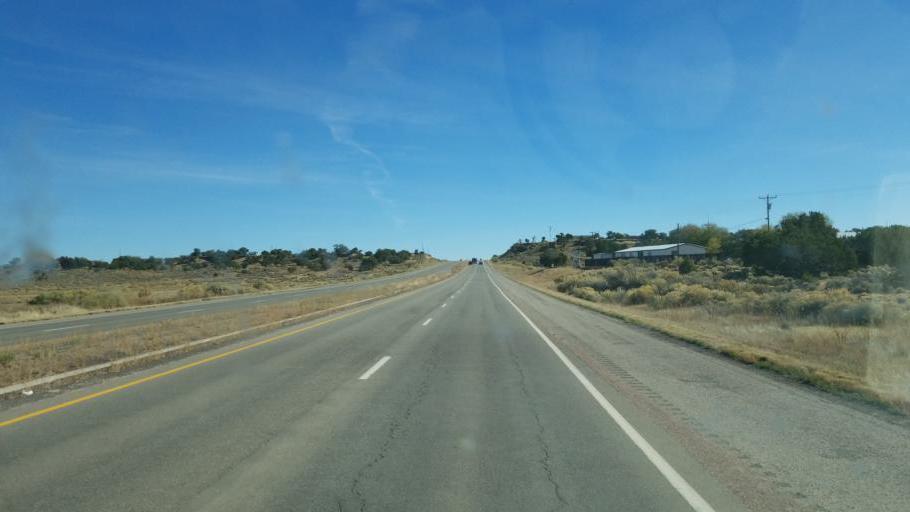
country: US
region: Arizona
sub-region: Apache County
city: Window Rock
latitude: 35.6313
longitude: -108.9086
